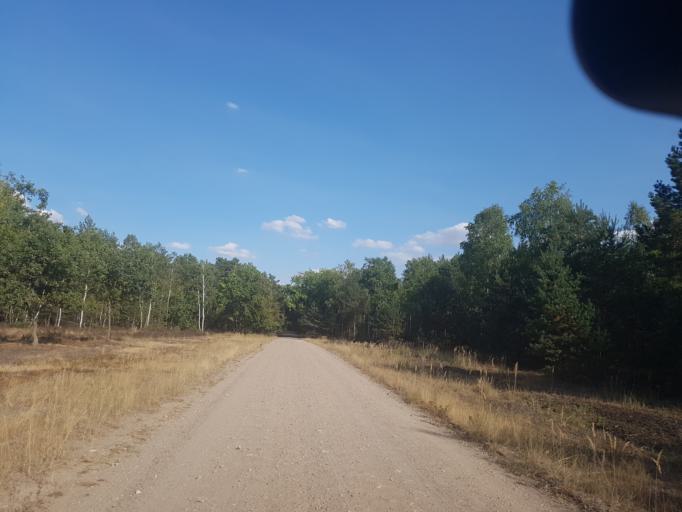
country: DE
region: Saxony-Anhalt
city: Jessen
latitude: 51.8707
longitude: 12.9975
